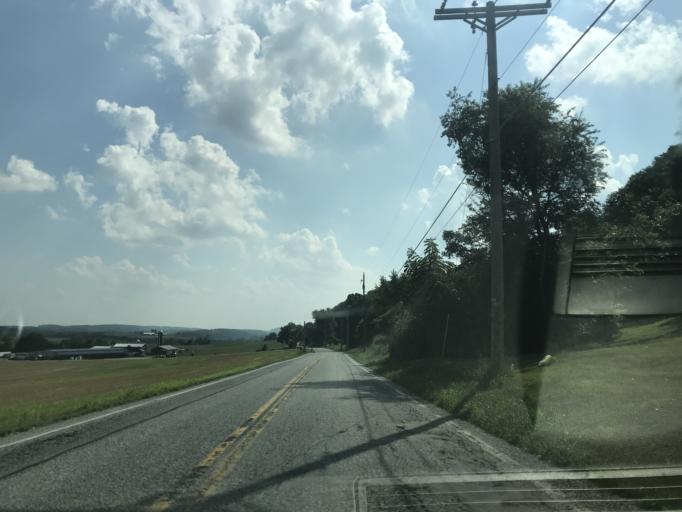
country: US
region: Pennsylvania
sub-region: York County
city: Glen Rock
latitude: 39.7402
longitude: -76.8152
